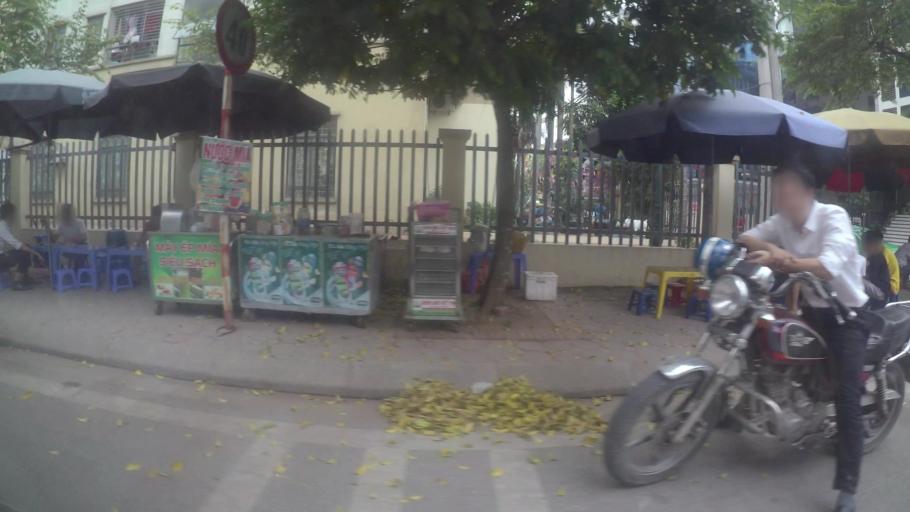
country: VN
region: Ha Noi
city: Cau Dien
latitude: 21.0331
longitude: 105.7620
